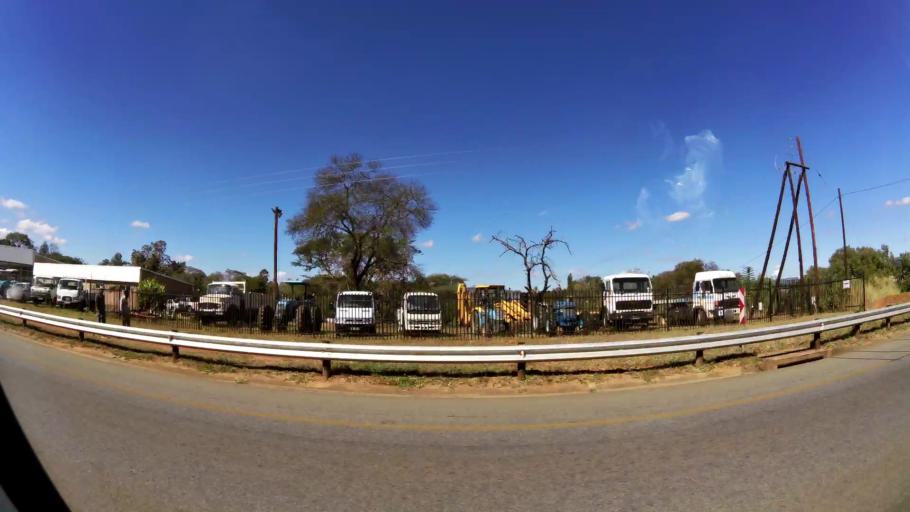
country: ZA
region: Limpopo
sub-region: Mopani District Municipality
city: Tzaneen
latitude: -23.8203
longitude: 30.1653
